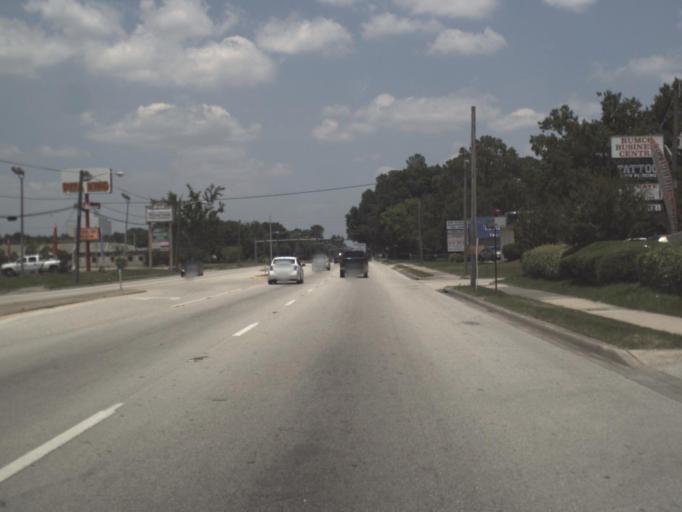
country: US
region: Florida
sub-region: Duval County
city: Jacksonville
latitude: 30.3376
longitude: -81.7310
